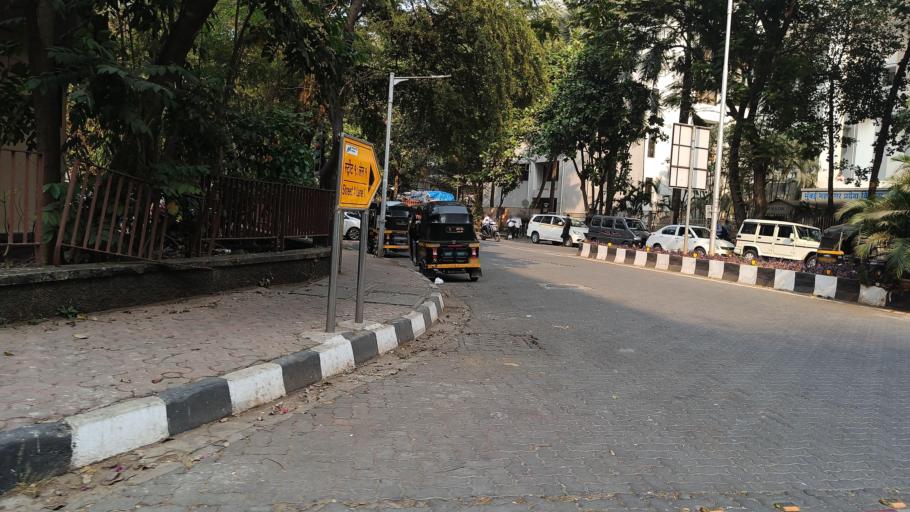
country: IN
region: Maharashtra
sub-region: Mumbai Suburban
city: Mumbai
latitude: 19.0552
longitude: 72.8512
